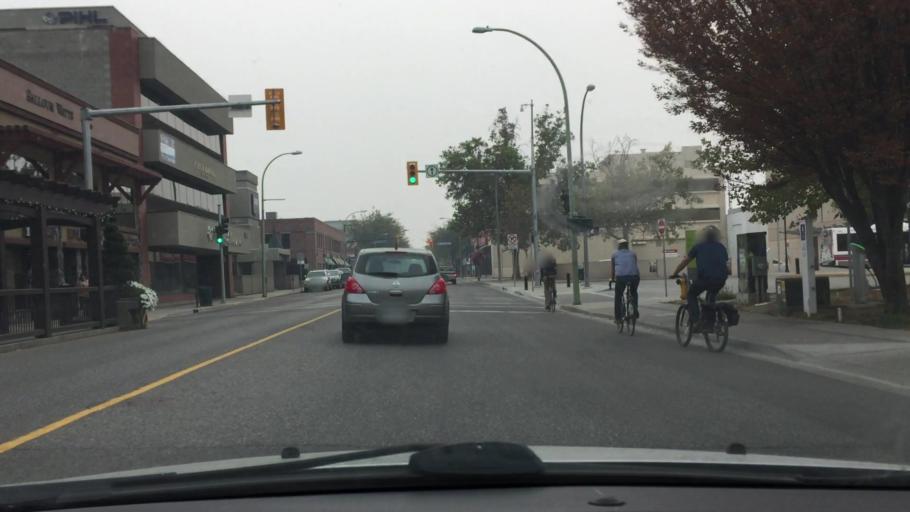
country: CA
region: British Columbia
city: Kelowna
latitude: 49.8877
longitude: -119.4936
